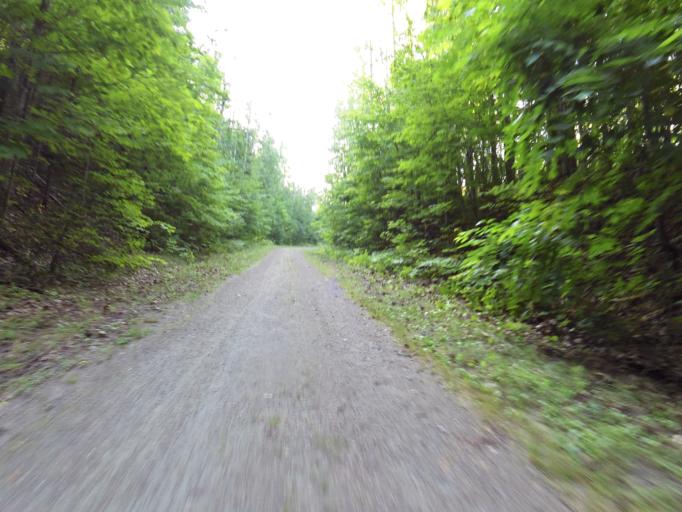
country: CA
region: Quebec
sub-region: Outaouais
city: Maniwaki
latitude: 46.2599
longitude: -76.0234
